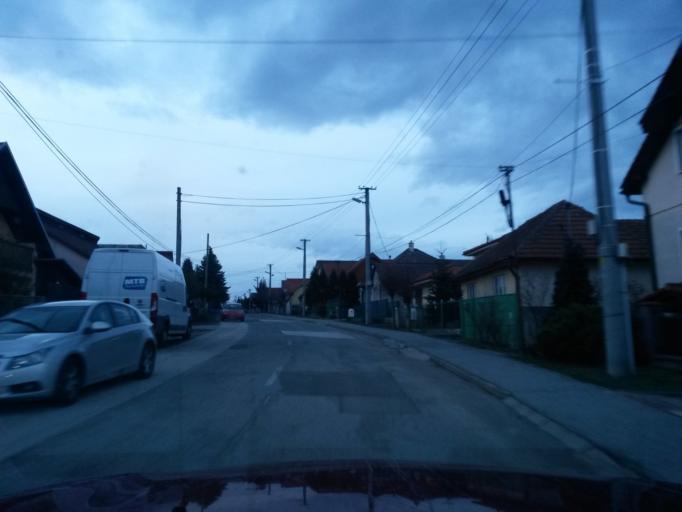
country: SK
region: Kosicky
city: Kosice
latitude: 48.7287
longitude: 21.3037
